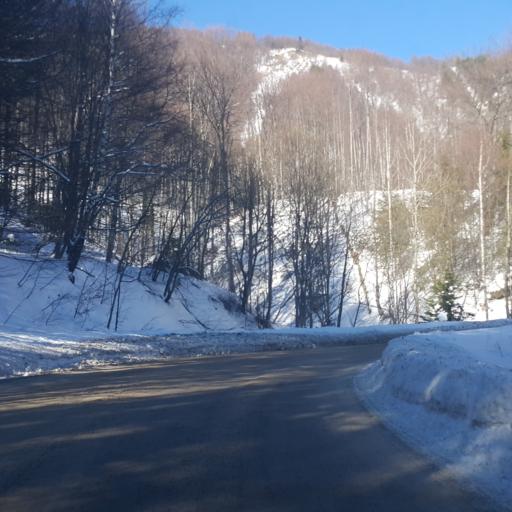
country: XK
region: Mitrovica
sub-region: Komuna e Leposaviqit
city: Leposaviq
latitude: 43.3089
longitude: 20.8565
